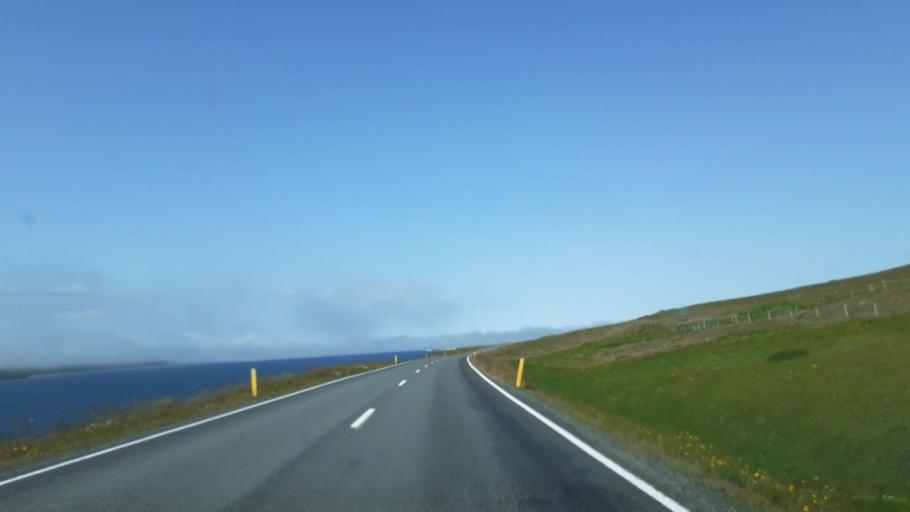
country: IS
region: West
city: Borgarnes
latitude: 65.2059
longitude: -21.0644
